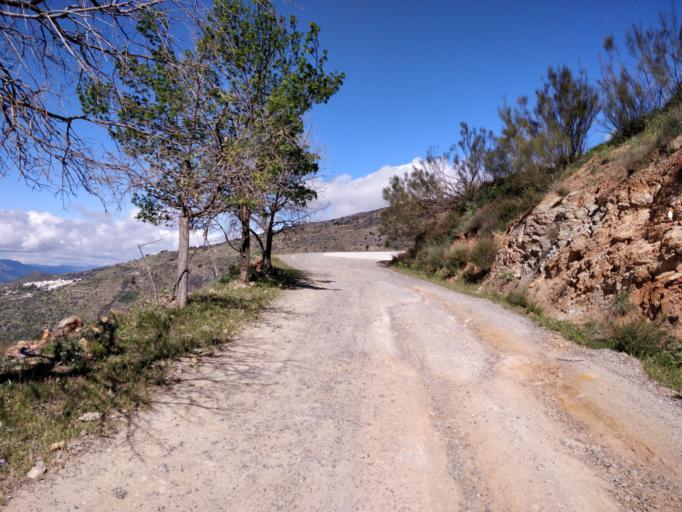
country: ES
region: Andalusia
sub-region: Provincia de Granada
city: Soportujar
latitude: 36.9289
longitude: -3.3983
